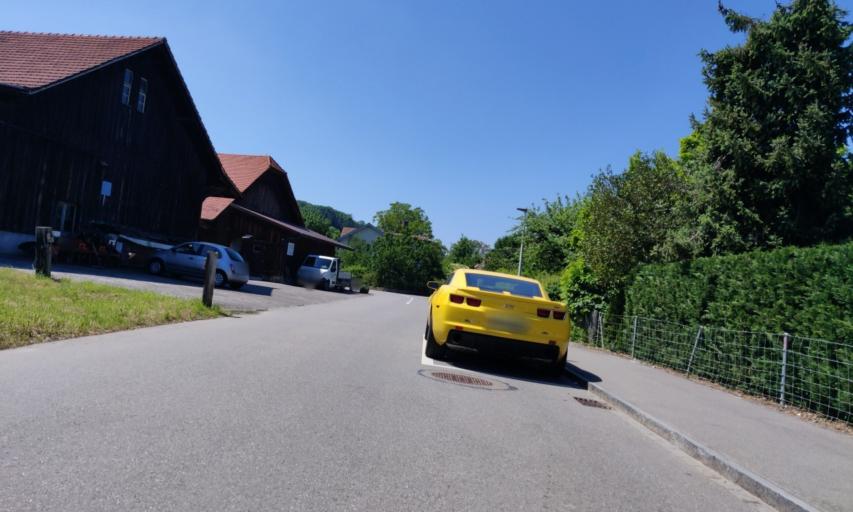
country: CH
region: Basel-Landschaft
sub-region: Bezirk Arlesheim
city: Aesch
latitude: 47.4678
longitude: 7.5908
